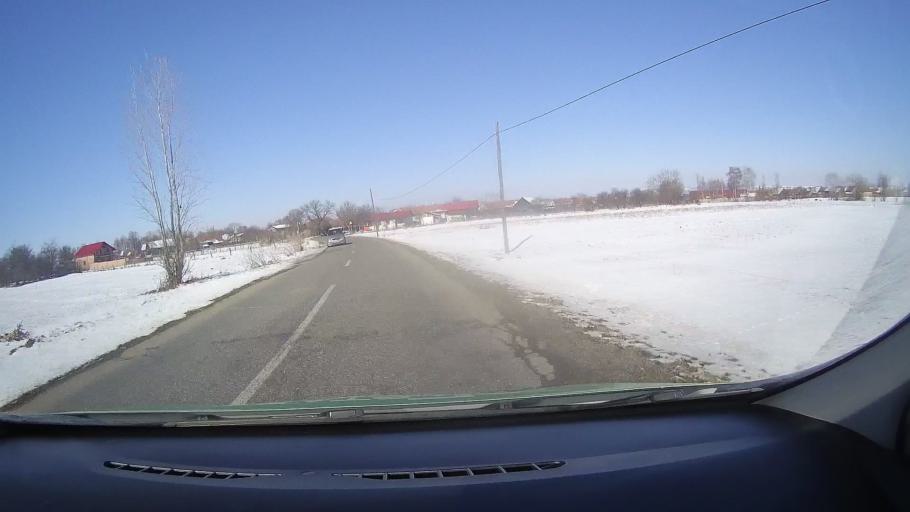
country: RO
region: Brasov
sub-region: Comuna Harseni
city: Harseni
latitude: 45.7840
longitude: 25.0010
